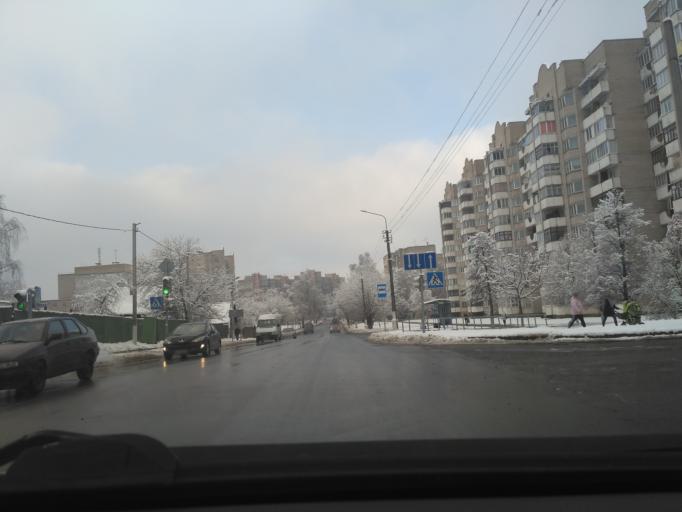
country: BY
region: Minsk
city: Horad Barysaw
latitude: 54.2180
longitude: 28.4983
